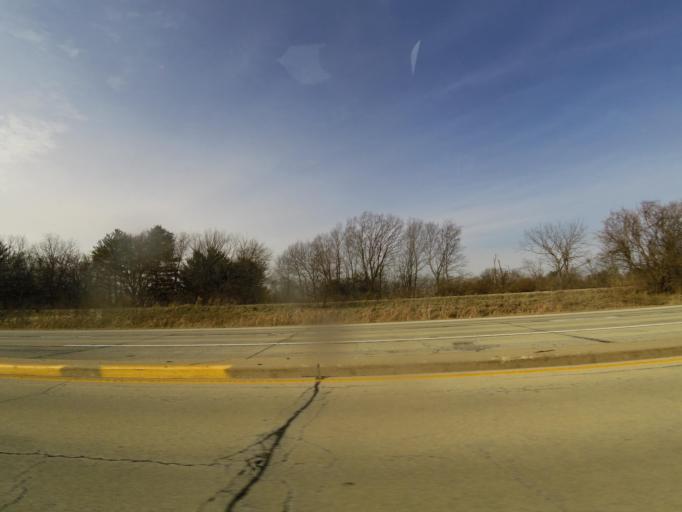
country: US
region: Illinois
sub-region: Macon County
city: Decatur
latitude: 39.7830
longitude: -88.9786
